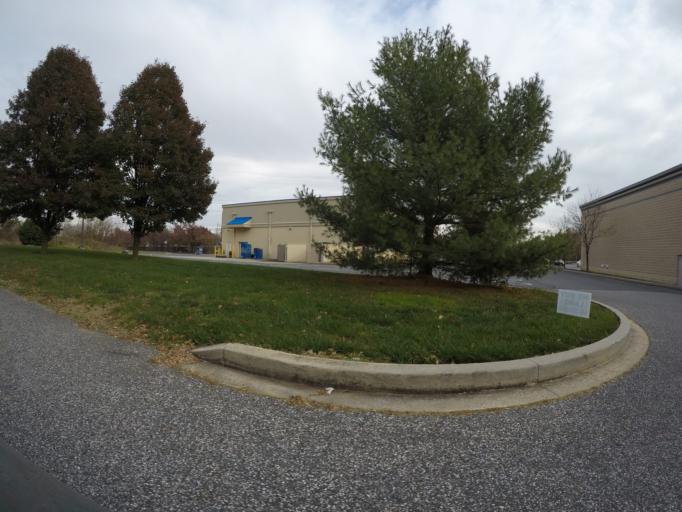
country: US
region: Maryland
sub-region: Harford County
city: Havre de Grace
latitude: 39.5459
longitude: -76.1088
